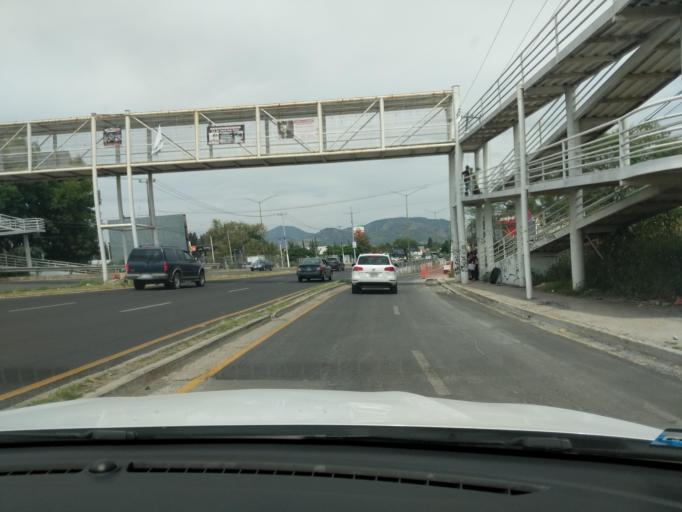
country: MX
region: Jalisco
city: Tesistan
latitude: 20.7925
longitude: -103.4769
